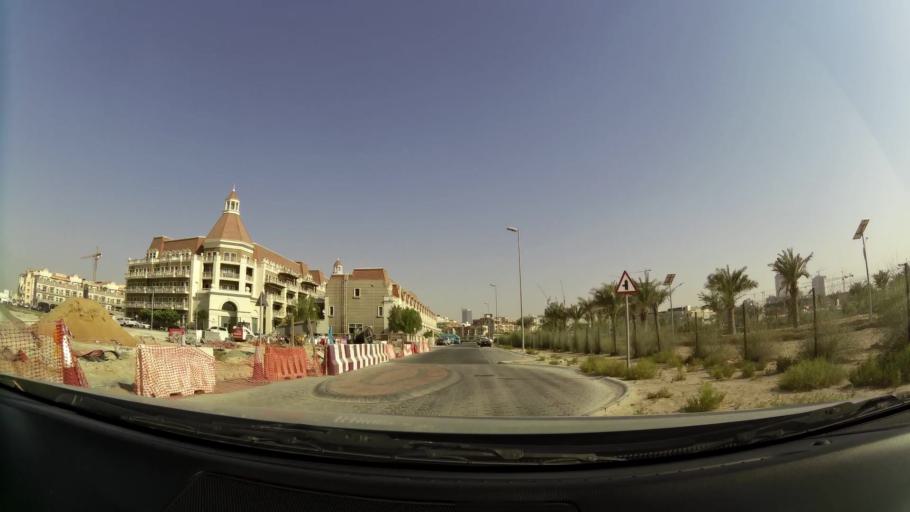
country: AE
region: Dubai
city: Dubai
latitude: 25.0654
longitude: 55.2062
